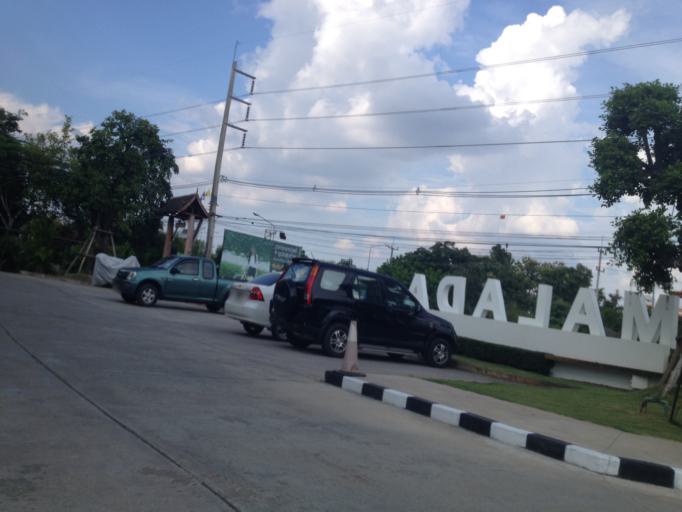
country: TH
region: Chiang Mai
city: Hang Dong
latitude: 18.7258
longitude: 98.9264
